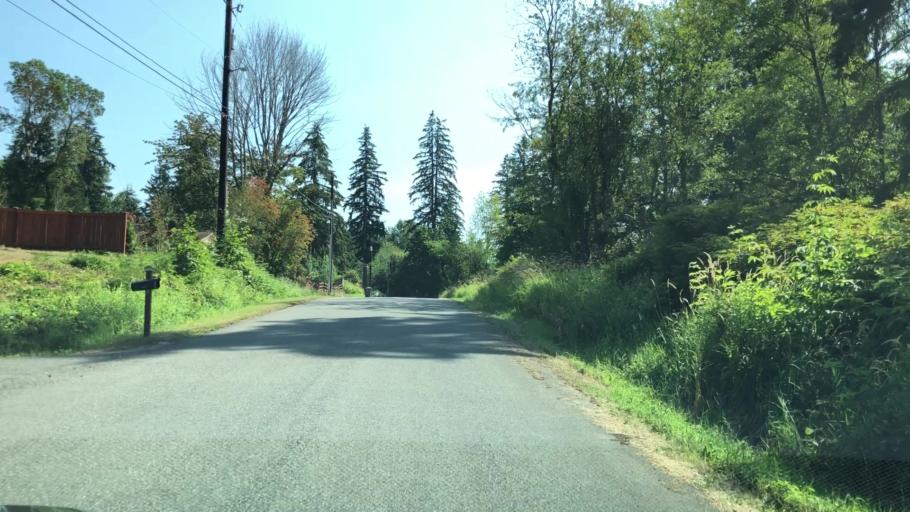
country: US
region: Washington
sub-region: Snohomish County
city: Maltby
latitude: 47.7816
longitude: -122.1371
